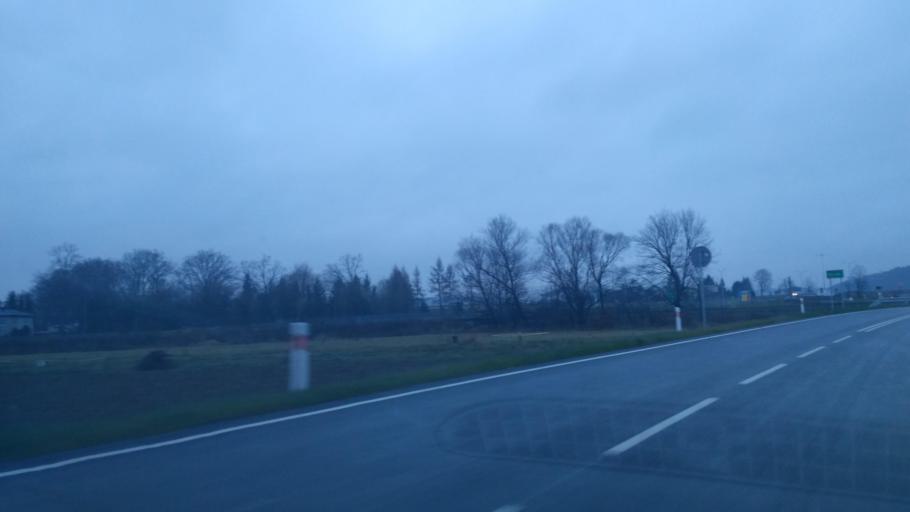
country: PL
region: Subcarpathian Voivodeship
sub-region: Powiat rzeszowski
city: Dynow
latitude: 49.8331
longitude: 22.2420
